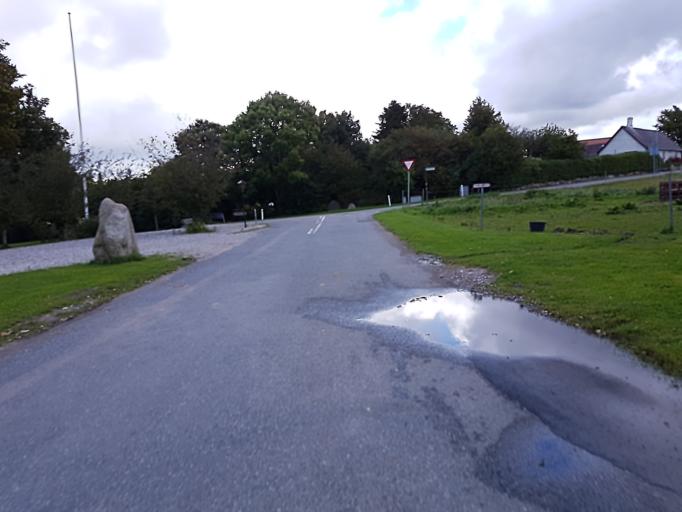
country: DK
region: Zealand
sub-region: Roskilde Kommune
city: Gundsomagle
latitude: 55.7200
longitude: 12.1590
